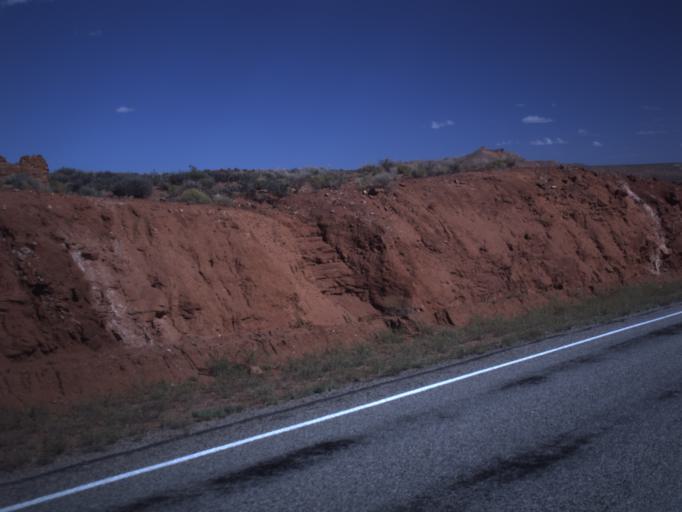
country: US
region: Utah
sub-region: Wayne County
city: Loa
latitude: 38.0644
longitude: -110.6008
